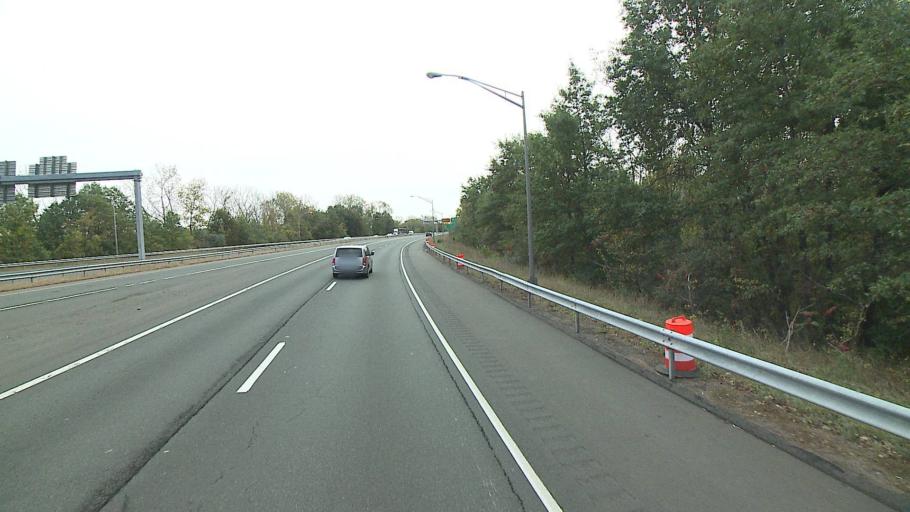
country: US
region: Connecticut
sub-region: Hartford County
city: Kensington
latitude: 41.6457
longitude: -72.7617
